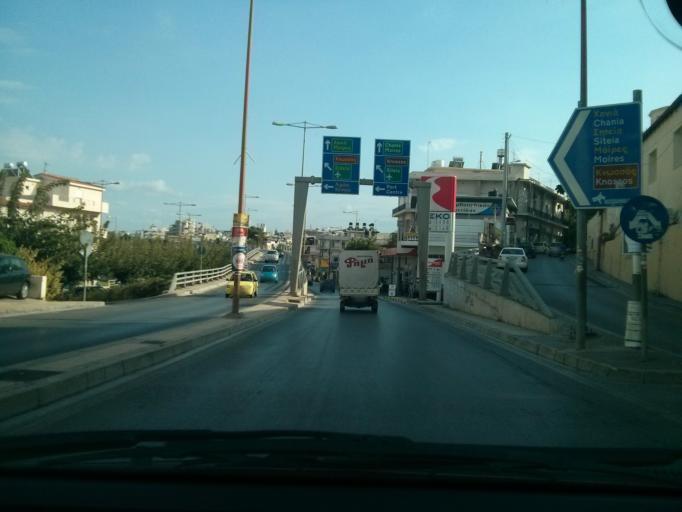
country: GR
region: Crete
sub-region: Nomos Irakleiou
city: Irakleion
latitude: 35.3278
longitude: 25.1380
